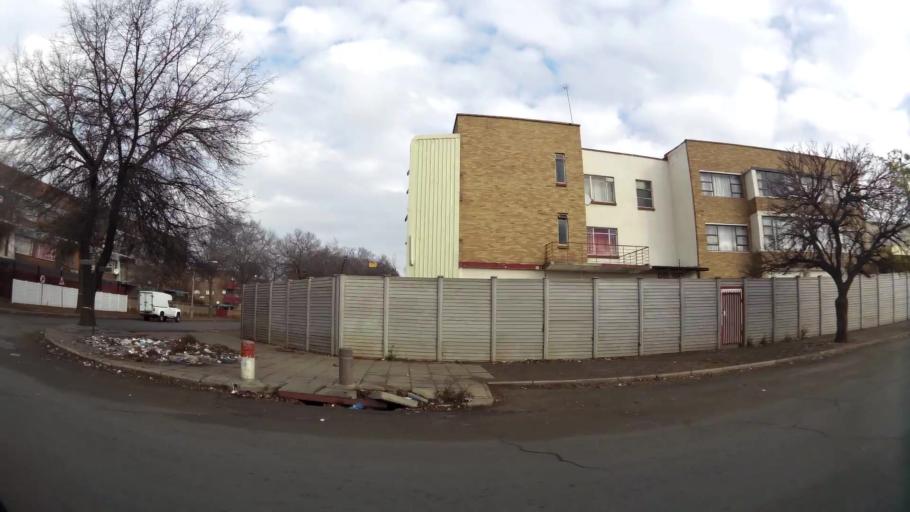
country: ZA
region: Gauteng
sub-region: Sedibeng District Municipality
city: Vanderbijlpark
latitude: -26.6949
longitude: 27.8252
